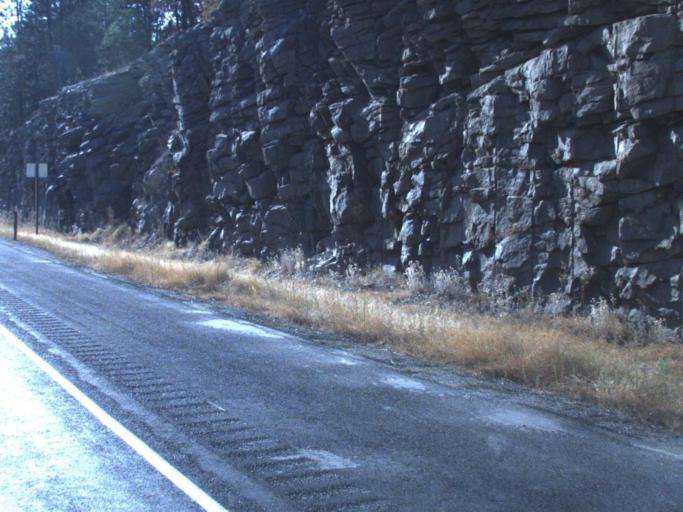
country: US
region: Washington
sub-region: Spokane County
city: Deer Park
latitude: 48.0978
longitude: -117.3055
